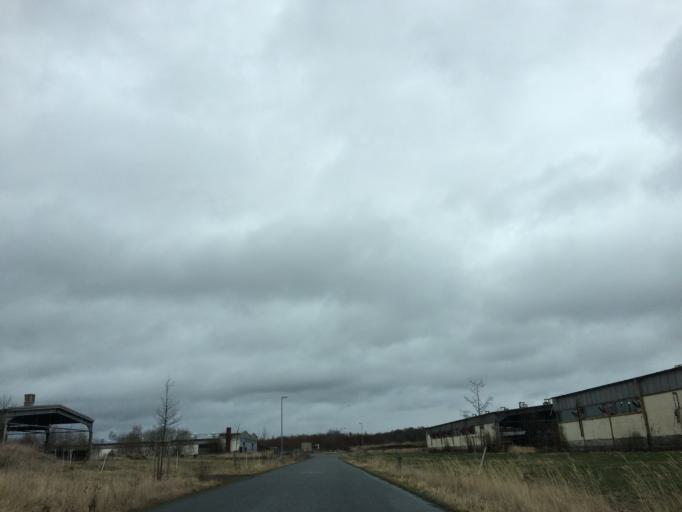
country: DE
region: Thuringia
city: Quaschwitz
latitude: 50.6813
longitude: 11.7170
